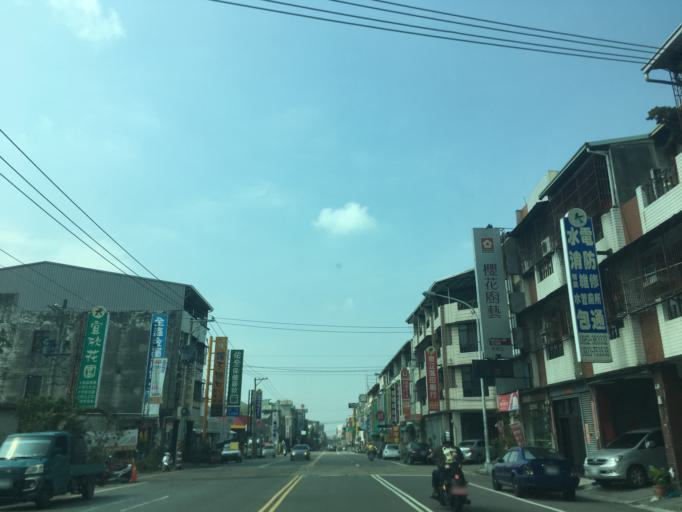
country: TW
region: Taiwan
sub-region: Taichung City
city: Taichung
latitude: 24.1553
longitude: 120.7120
